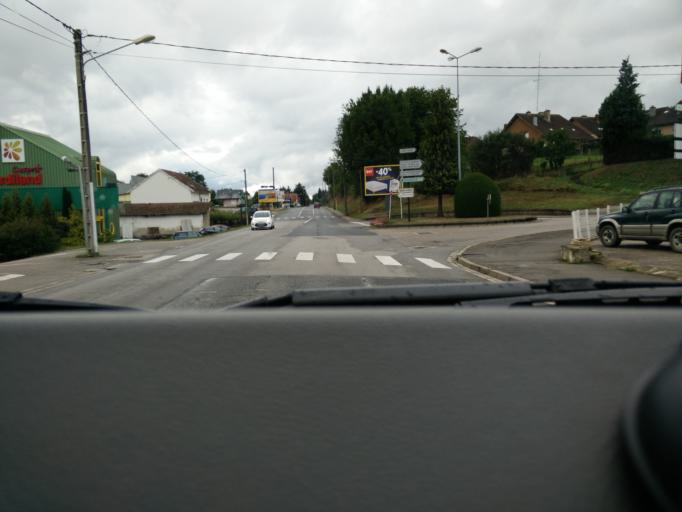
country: FR
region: Lorraine
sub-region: Departement des Vosges
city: Saint-Die-des-Vosges
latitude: 48.2949
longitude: 6.9383
